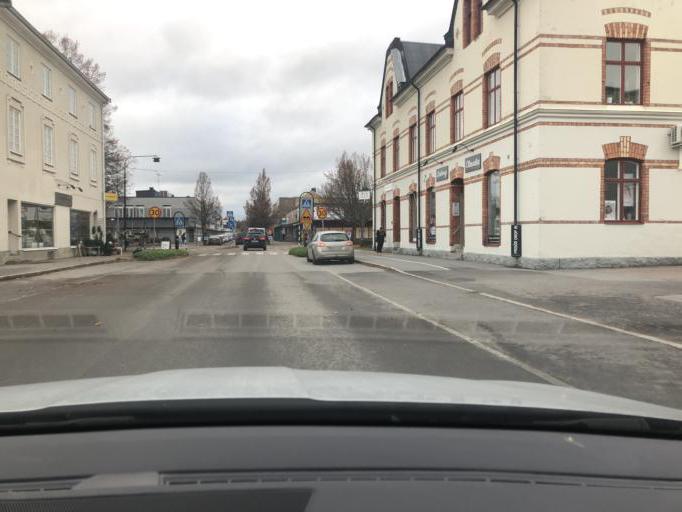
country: SE
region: Uppsala
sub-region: Tierps Kommun
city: Tierp
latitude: 60.3431
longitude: 17.5160
